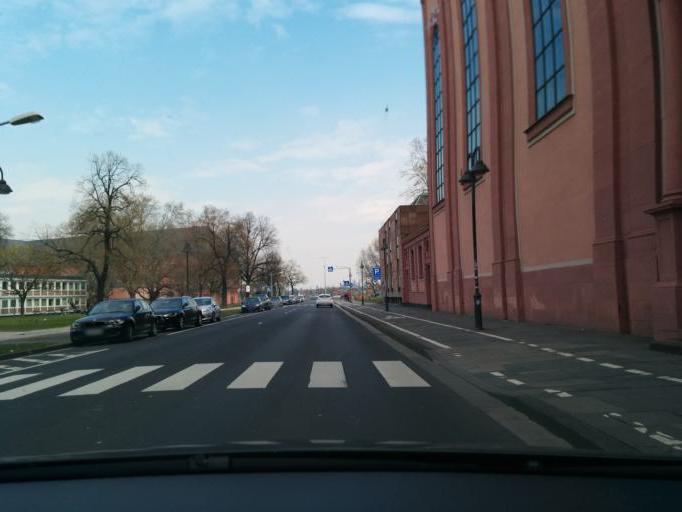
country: DE
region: Rheinland-Pfalz
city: Mainz
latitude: 50.0048
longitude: 8.2694
